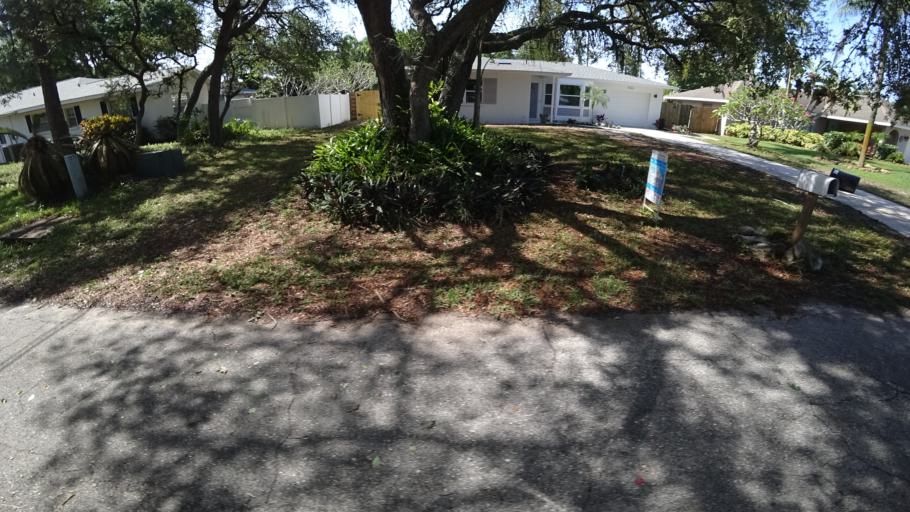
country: US
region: Florida
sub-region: Manatee County
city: West Bradenton
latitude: 27.5009
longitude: -82.6162
